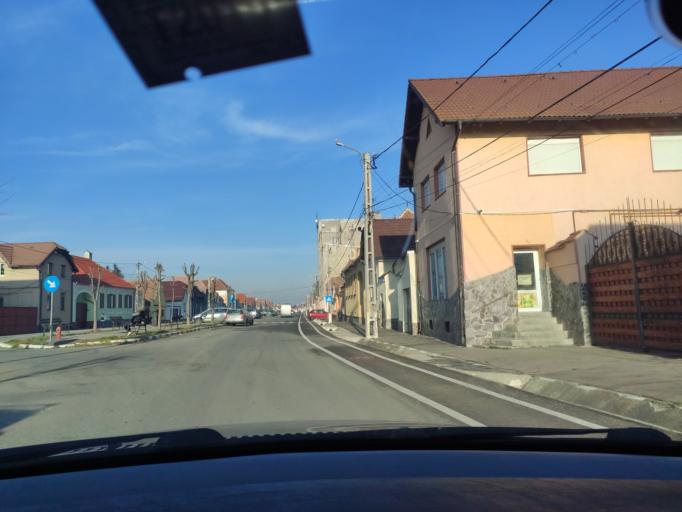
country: RO
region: Brasov
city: Codlea
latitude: 45.6983
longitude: 25.4494
